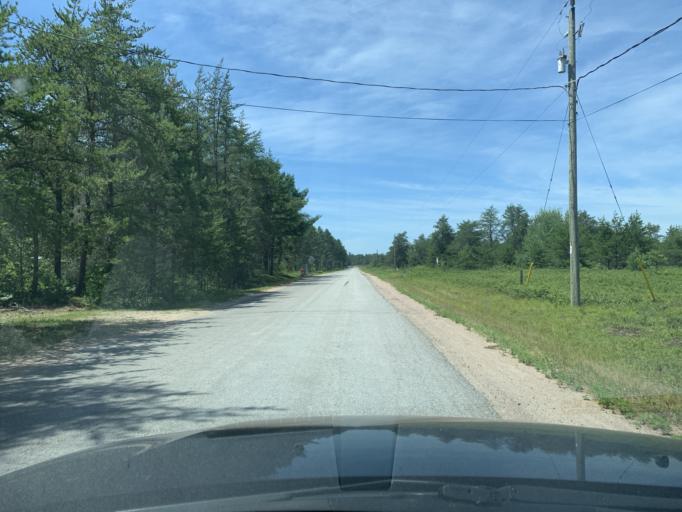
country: CA
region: Ontario
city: Petawawa
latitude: 45.6594
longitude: -77.5820
